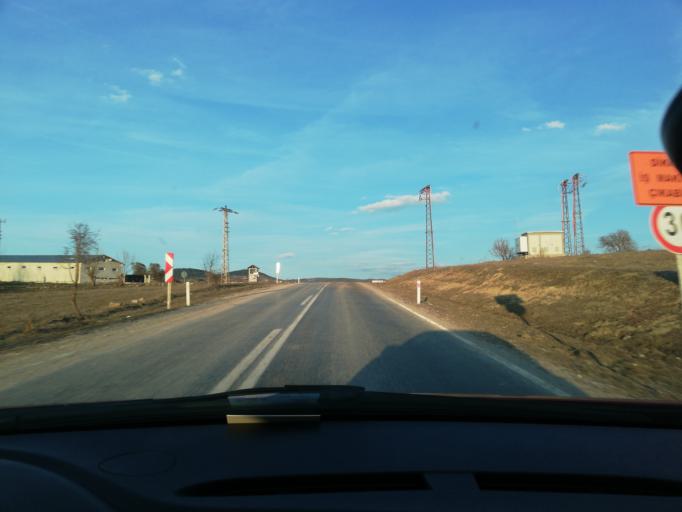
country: TR
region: Kastamonu
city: Agli
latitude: 41.6939
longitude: 33.6049
